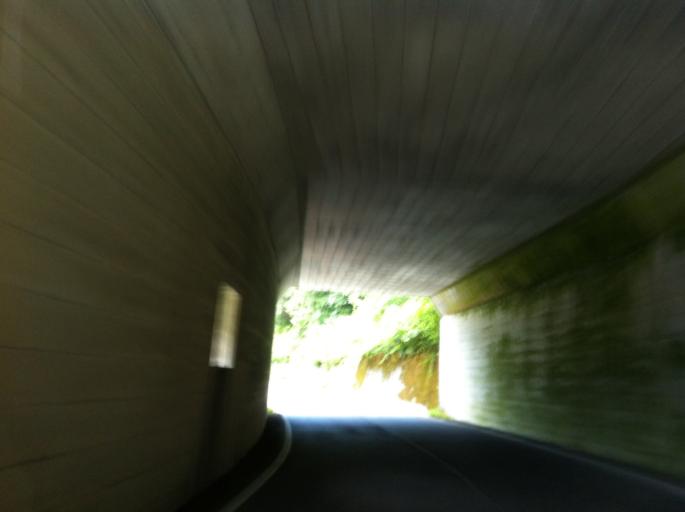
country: JP
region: Shizuoka
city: Shizuoka-shi
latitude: 35.1870
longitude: 138.3614
